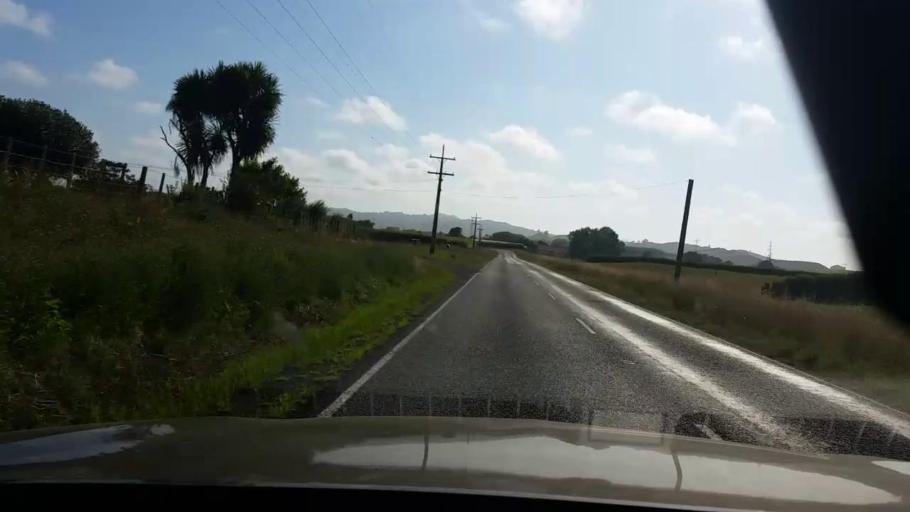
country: NZ
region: Waikato
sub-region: Hamilton City
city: Hamilton
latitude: -37.5915
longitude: 175.3837
